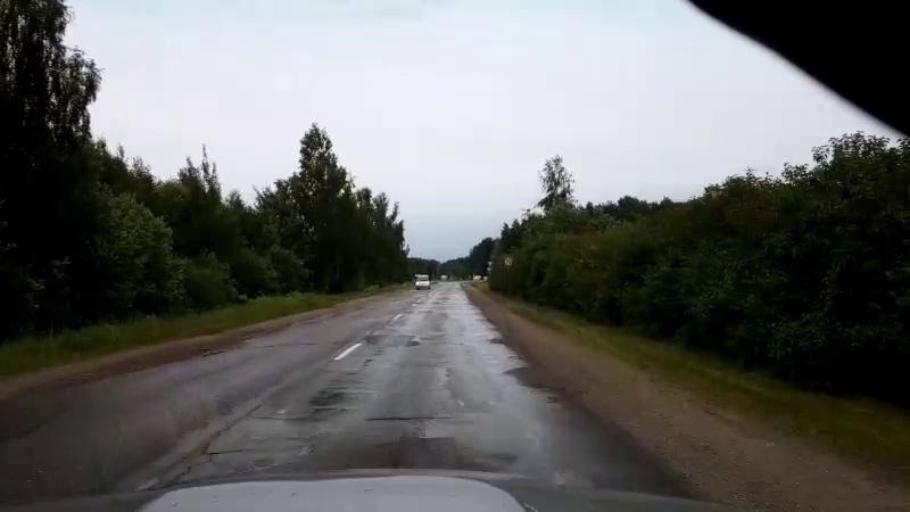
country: LV
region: Kekava
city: Kekava
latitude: 56.8114
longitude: 24.2719
